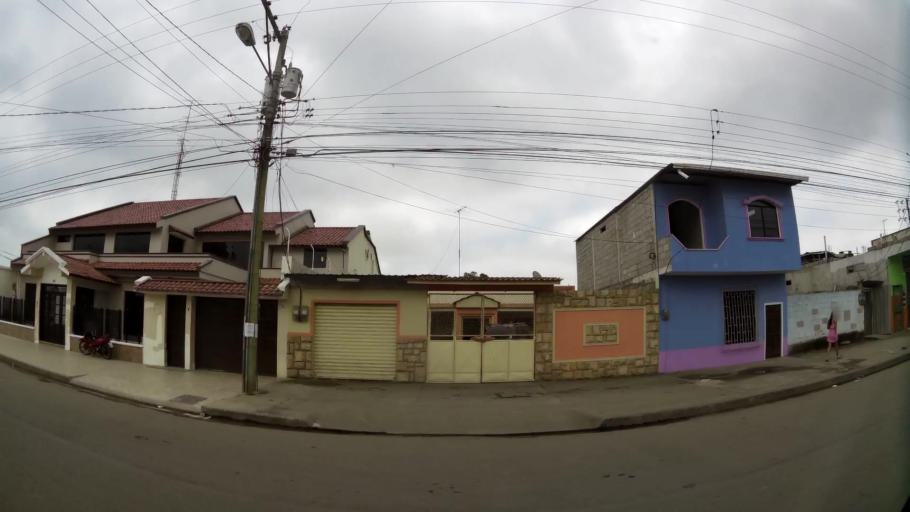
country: EC
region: El Oro
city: Pasaje
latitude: -3.2449
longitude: -79.8345
